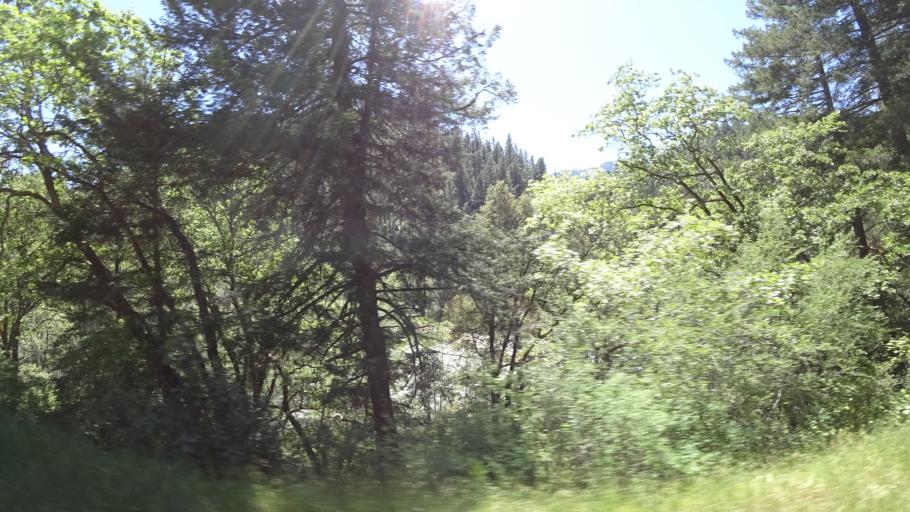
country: US
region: California
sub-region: Trinity County
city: Hayfork
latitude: 40.7494
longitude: -123.2749
